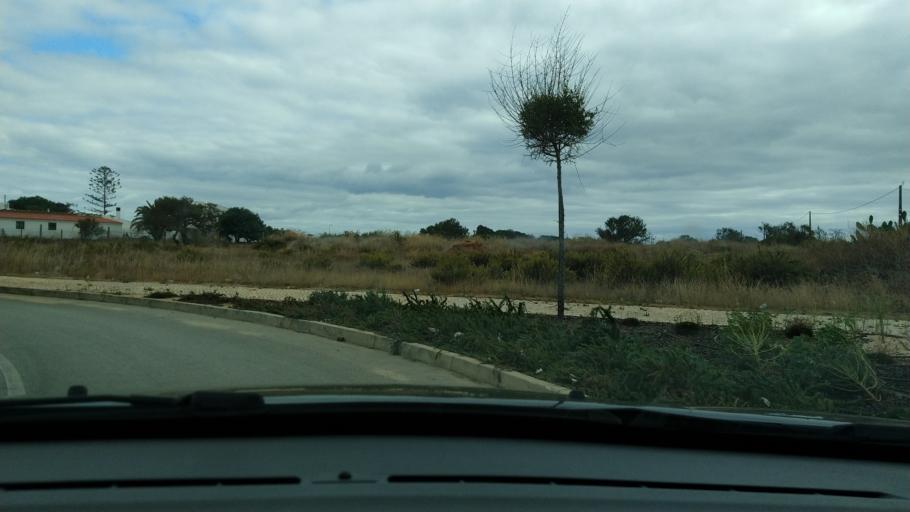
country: PT
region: Faro
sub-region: Lagos
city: Lagos
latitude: 37.0861
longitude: -8.6729
